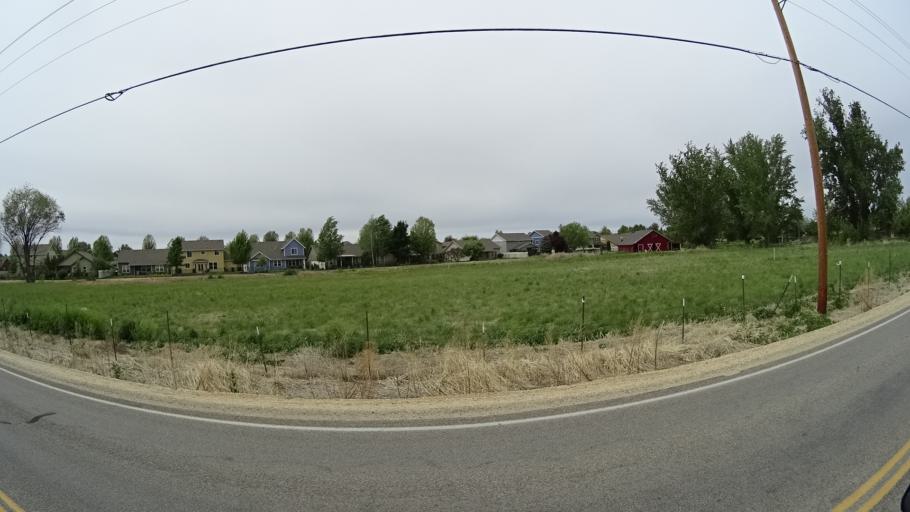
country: US
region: Idaho
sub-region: Ada County
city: Meridian
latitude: 43.5744
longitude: -116.3745
